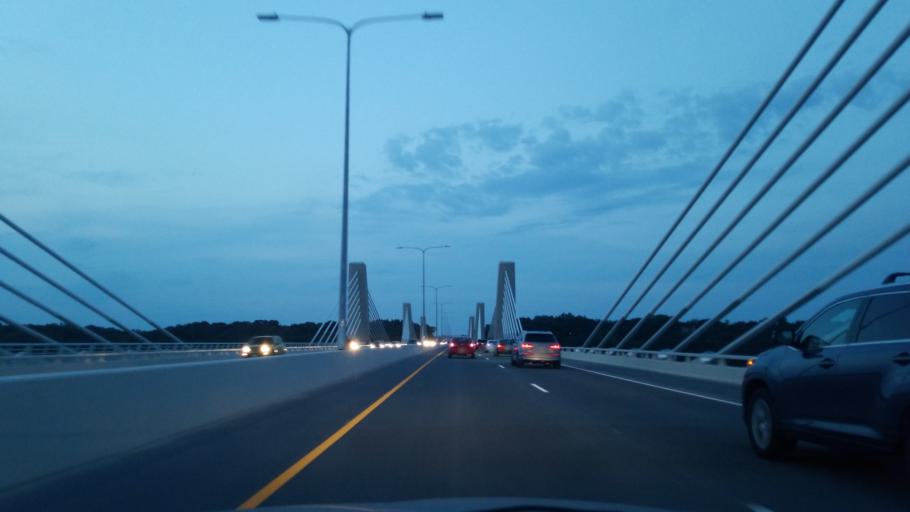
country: US
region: Minnesota
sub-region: Washington County
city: Oak Park Heights
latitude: 45.0408
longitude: -92.7860
